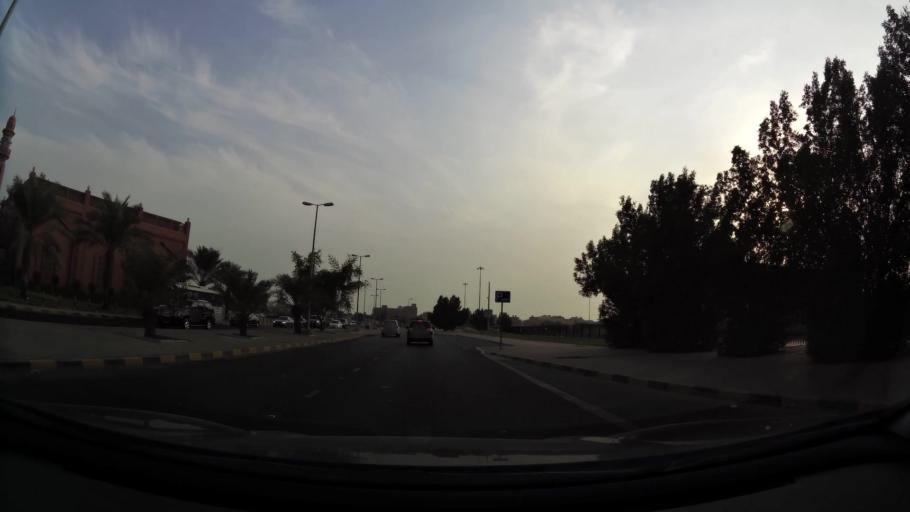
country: KW
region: Muhafazat Hawalli
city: As Salimiyah
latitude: 29.3281
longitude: 48.0783
